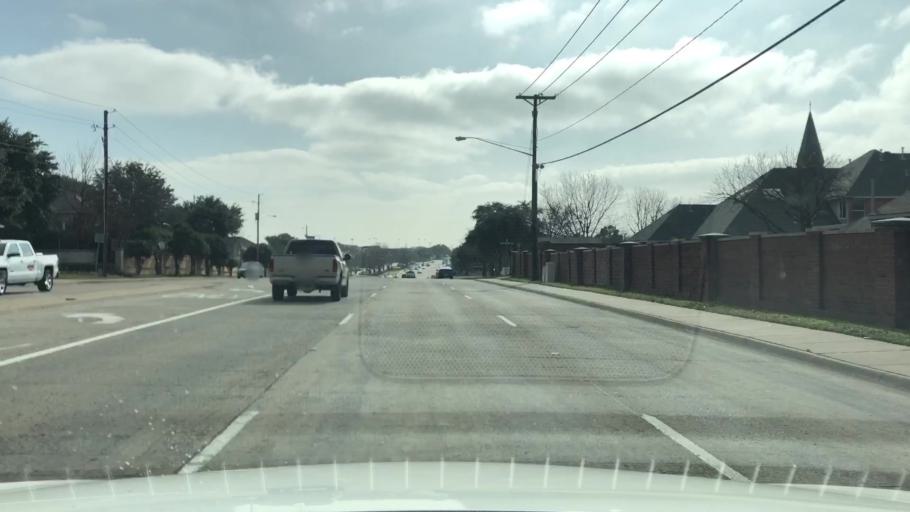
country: US
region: Texas
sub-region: Dallas County
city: Addison
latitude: 32.9922
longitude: -96.8551
